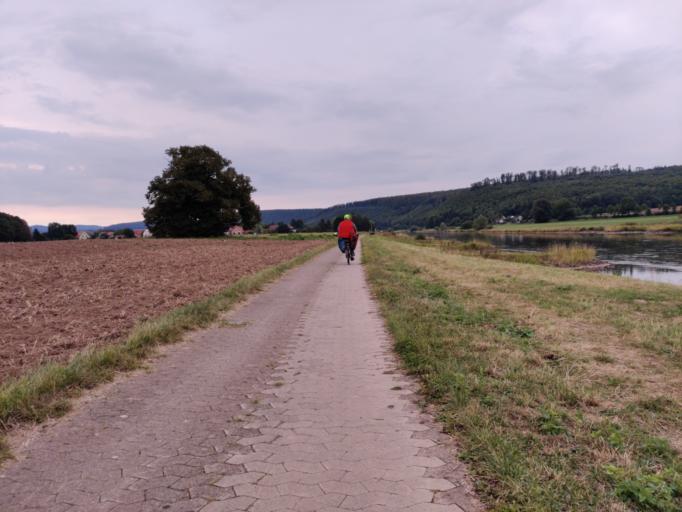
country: DE
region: Lower Saxony
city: Hehlen
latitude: 52.0076
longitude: 9.4306
